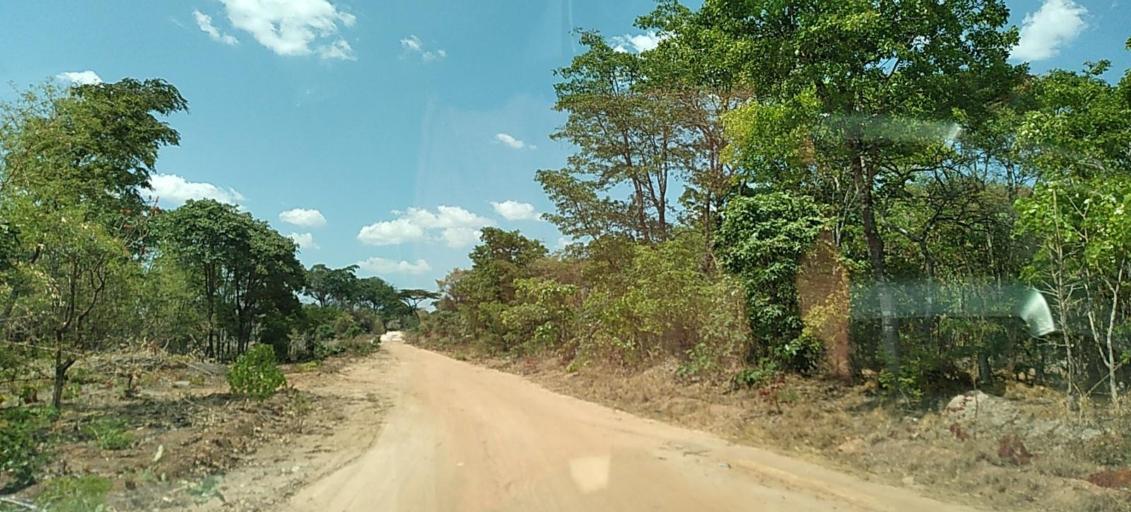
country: ZM
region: Copperbelt
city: Chililabombwe
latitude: -12.3872
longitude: 27.9174
